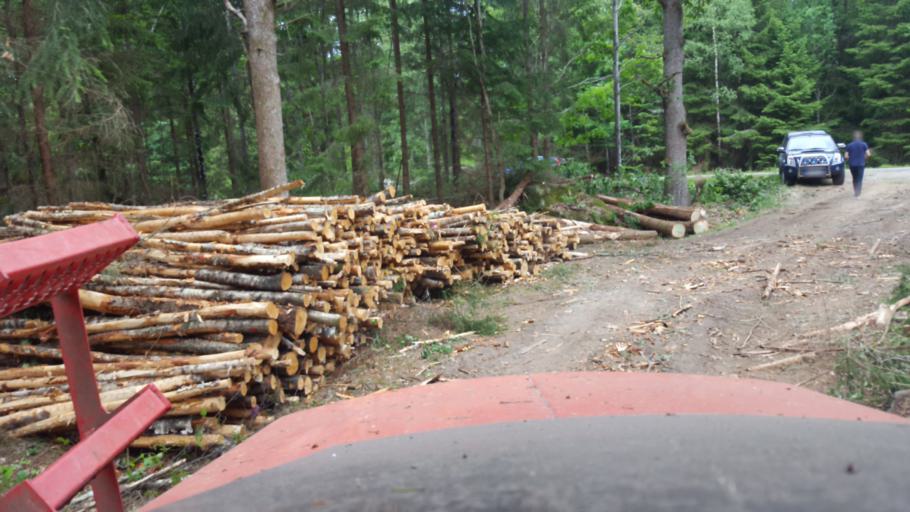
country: SE
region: Joenkoeping
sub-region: Varnamo Kommun
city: Bor
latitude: 57.0764
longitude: 14.2321
